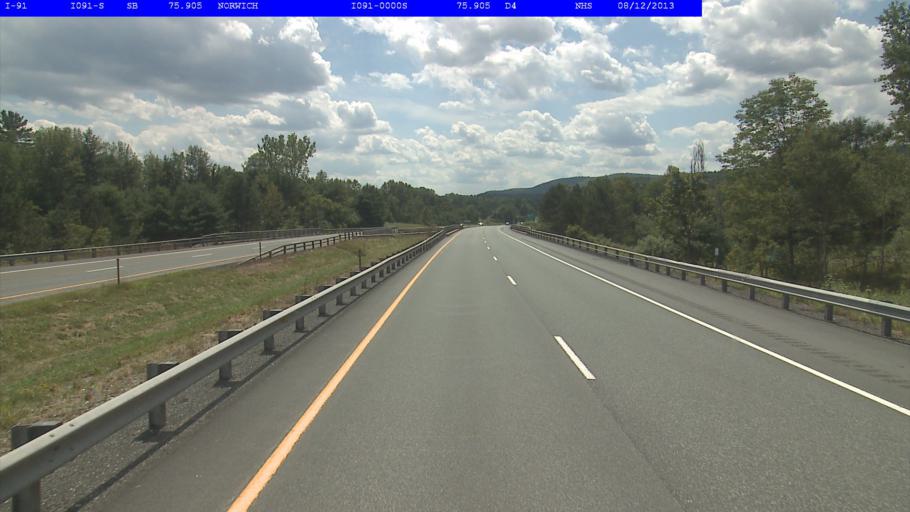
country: US
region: New Hampshire
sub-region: Grafton County
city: Hanover
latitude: 43.7178
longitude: -72.2930
